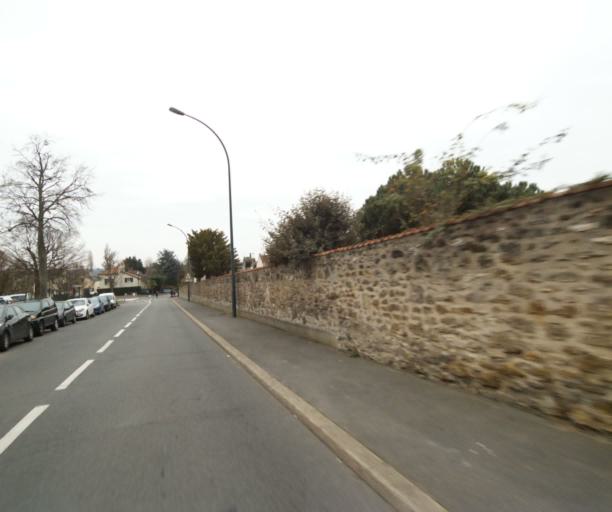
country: FR
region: Ile-de-France
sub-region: Departement des Hauts-de-Seine
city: Saint-Cloud
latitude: 48.8478
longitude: 2.1951
